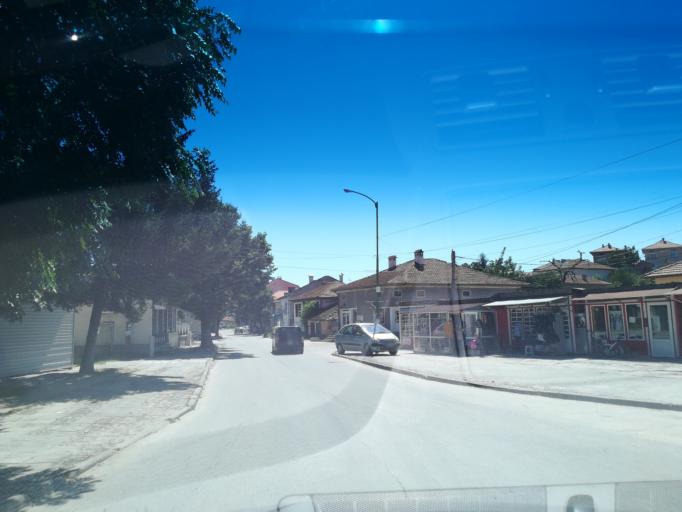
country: BG
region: Pazardzhik
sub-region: Obshtina Strelcha
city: Strelcha
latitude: 42.5054
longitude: 24.3209
